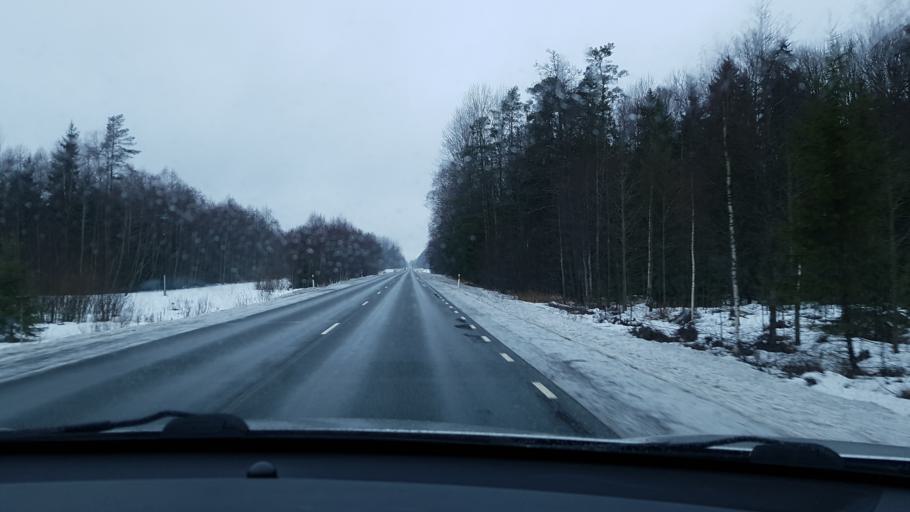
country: EE
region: Jaervamaa
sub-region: Tueri vald
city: Sarevere
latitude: 58.8031
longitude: 25.2245
